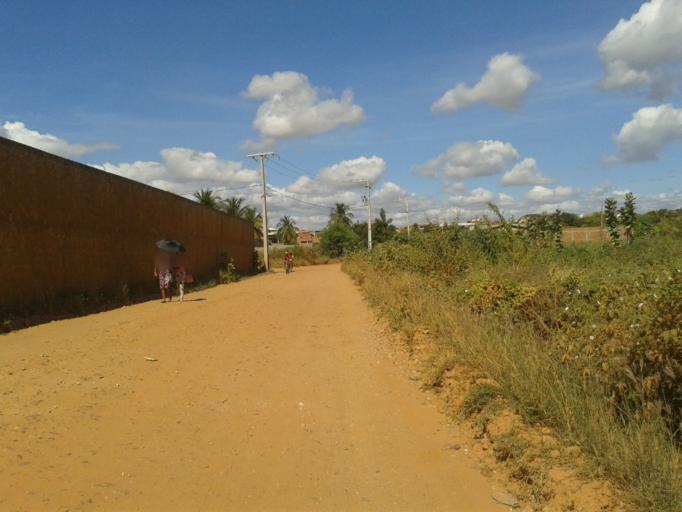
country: BR
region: Bahia
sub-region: Livramento Do Brumado
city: Livramento do Brumado
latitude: -13.6534
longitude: -41.8451
